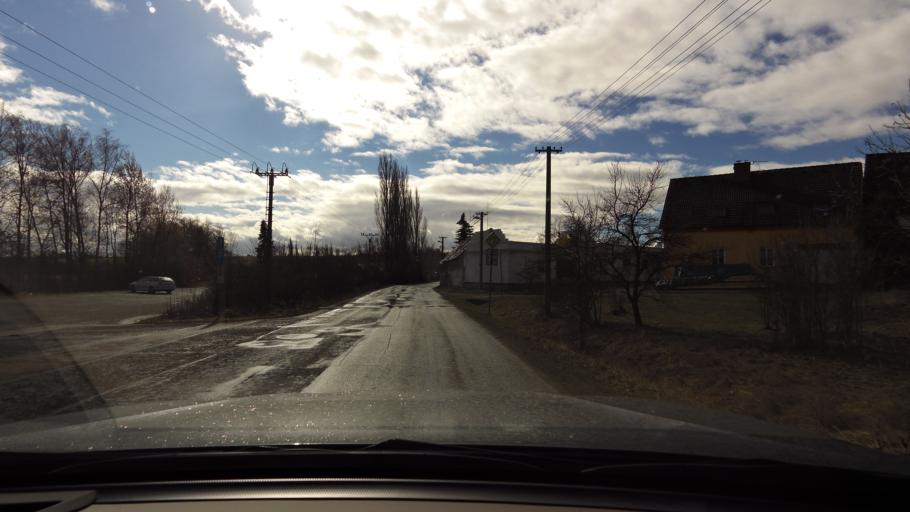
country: CZ
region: Plzensky
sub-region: Okres Plzen-Mesto
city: Pilsen
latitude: 49.7771
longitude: 13.3897
